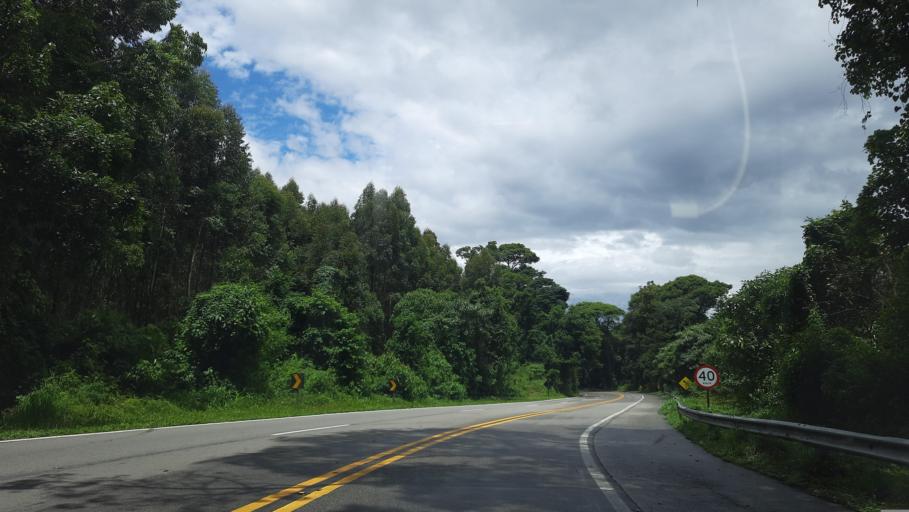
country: BR
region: Minas Gerais
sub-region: Pocos De Caldas
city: Pocos de Caldas
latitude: -21.8435
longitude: -46.6979
